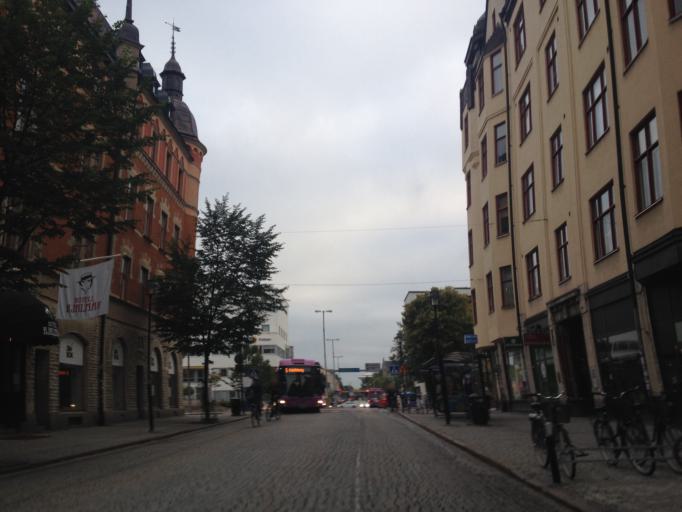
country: SE
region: OErebro
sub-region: Orebro Kommun
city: Orebro
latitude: 59.2772
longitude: 15.2159
